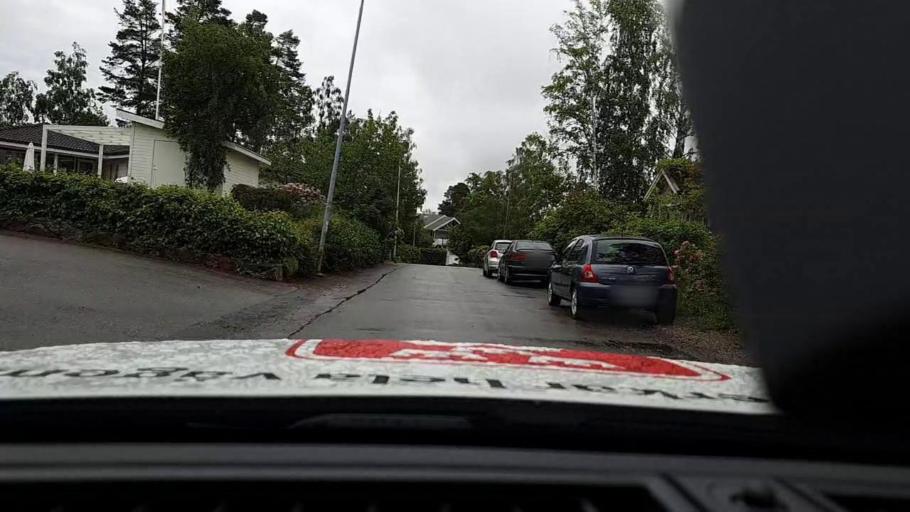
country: SE
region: Stockholm
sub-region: Taby Kommun
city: Taby
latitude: 59.4423
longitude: 18.0263
